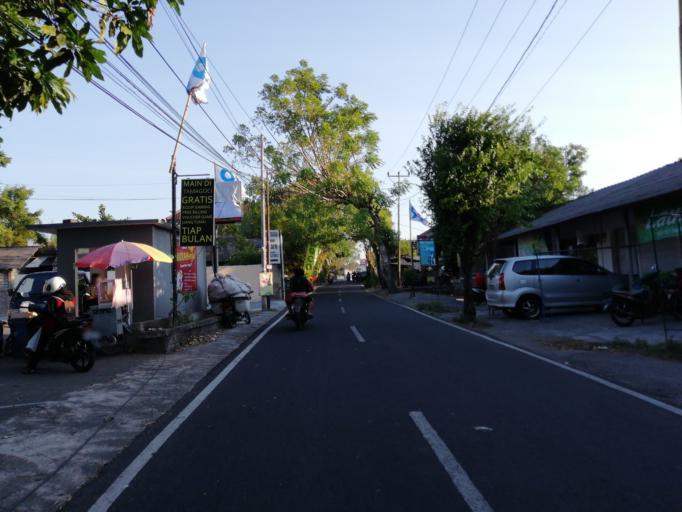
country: ID
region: Bali
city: Bualu
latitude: -8.7872
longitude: 115.1970
